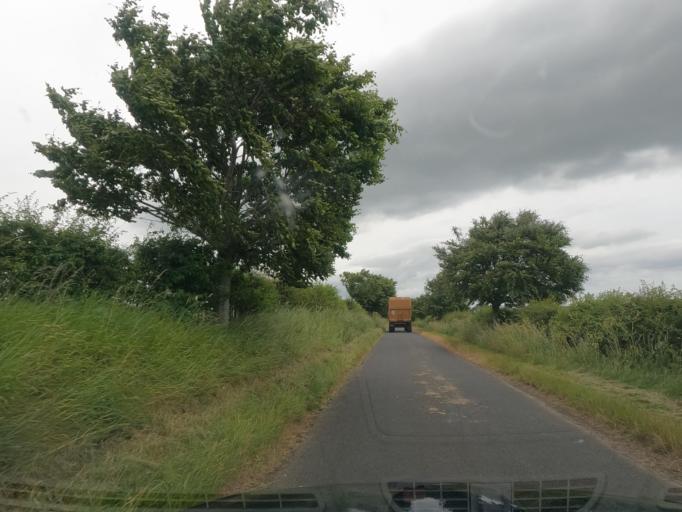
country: GB
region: England
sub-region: Northumberland
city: Lowick
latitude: 55.5815
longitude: -1.9220
